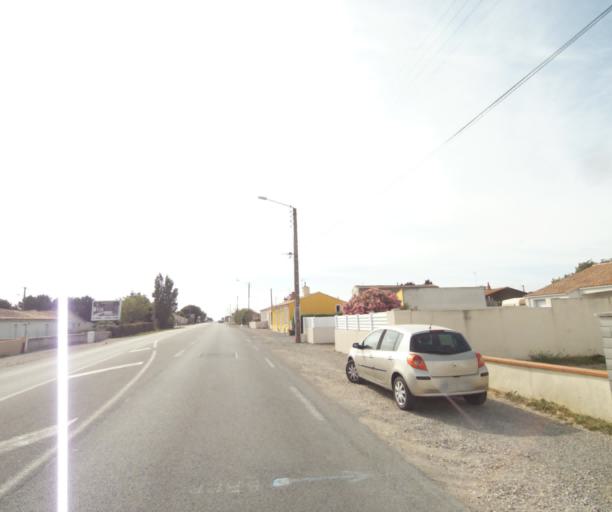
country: FR
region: Pays de la Loire
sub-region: Departement de la Vendee
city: Chateau-d'Olonne
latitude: 46.4841
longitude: -1.7276
